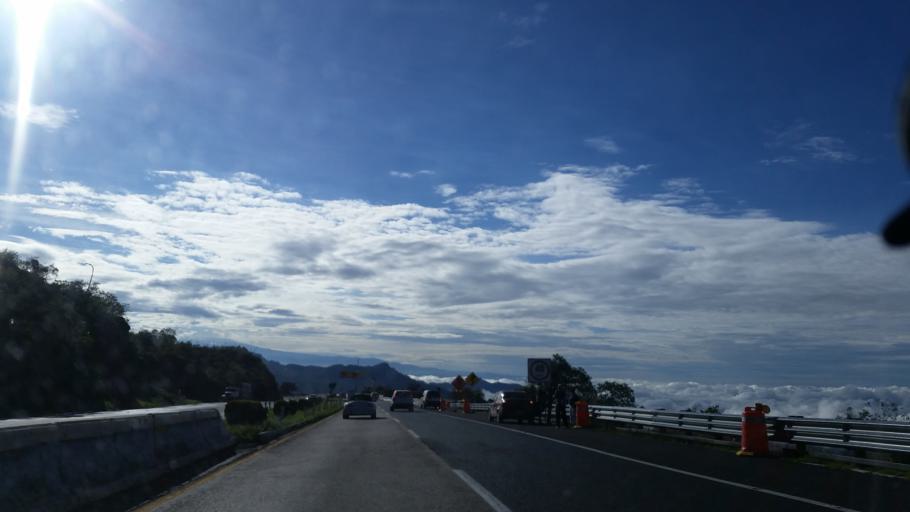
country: MX
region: Morelos
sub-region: Cuernavaca
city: Villa Santiago
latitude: 19.0197
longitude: -99.1550
